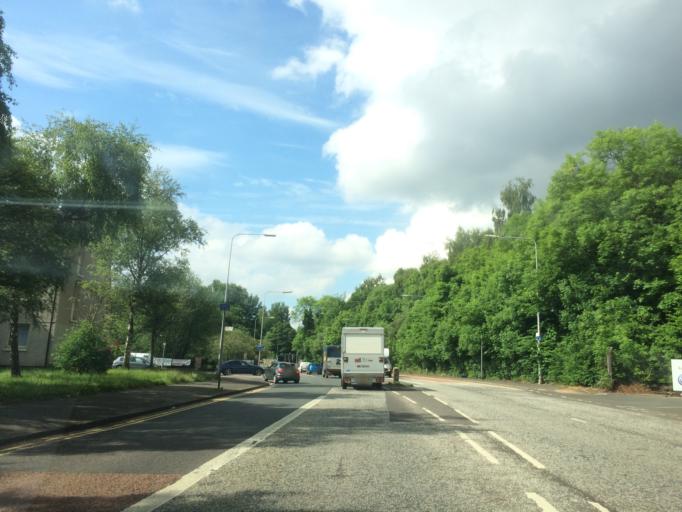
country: GB
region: Scotland
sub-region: East Renfrewshire
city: Giffnock
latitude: 55.8264
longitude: -4.2979
